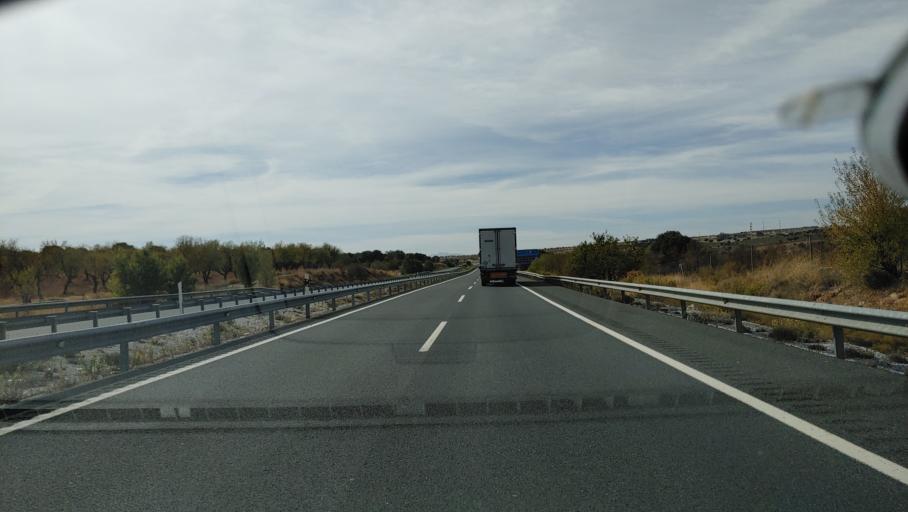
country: ES
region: Andalusia
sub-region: Provincia de Granada
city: Gor
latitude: 37.4014
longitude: -2.9312
